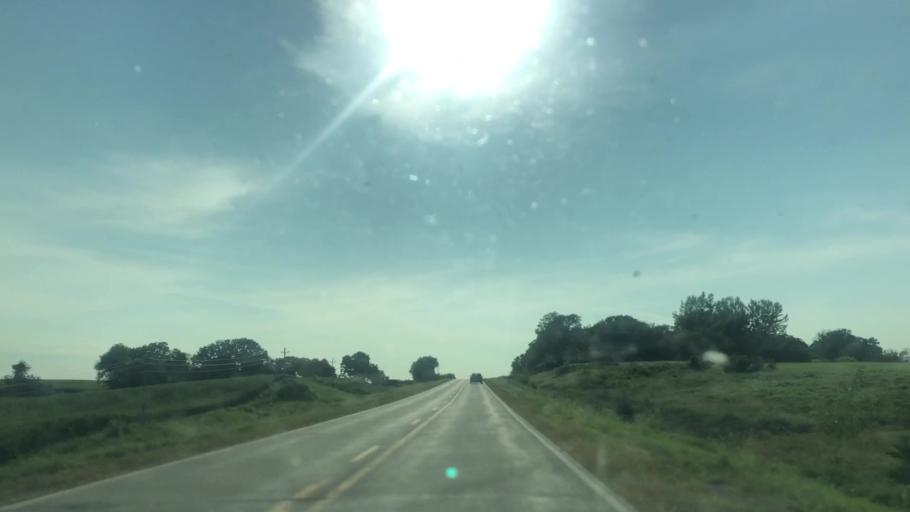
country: US
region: Iowa
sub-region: Marshall County
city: Marshalltown
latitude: 42.0490
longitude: -92.9808
